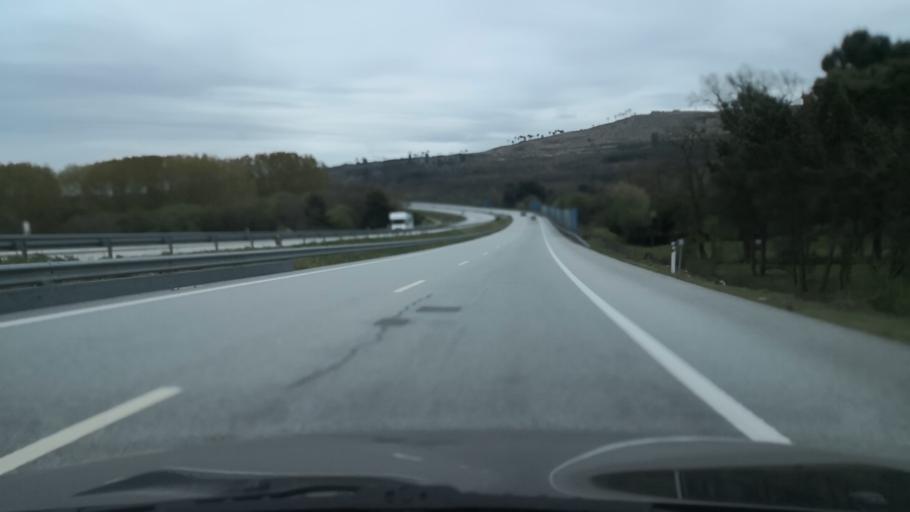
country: PT
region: Viseu
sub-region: Mangualde
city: Mangualde
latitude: 40.6152
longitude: -7.7171
